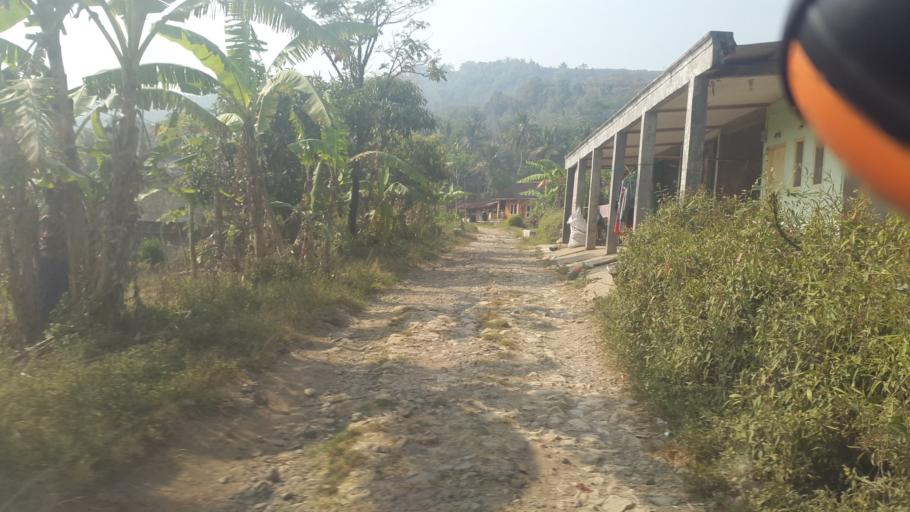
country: ID
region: West Java
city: Suryabakti
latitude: -7.0284
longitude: 106.8531
